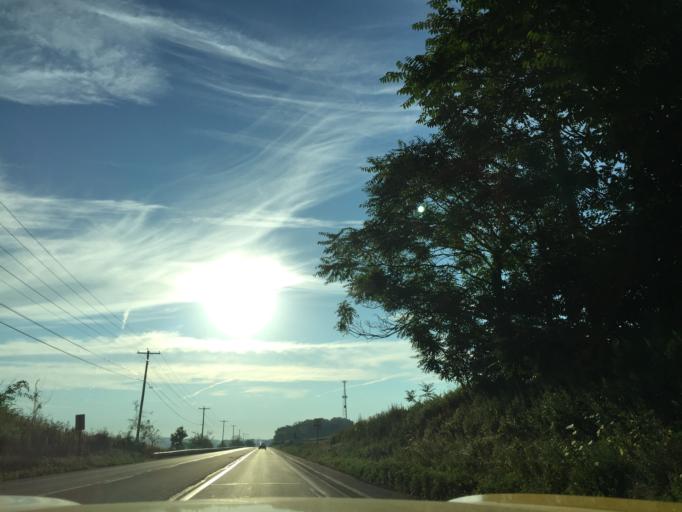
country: US
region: Pennsylvania
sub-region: Berks County
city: Topton
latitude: 40.5405
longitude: -75.7122
